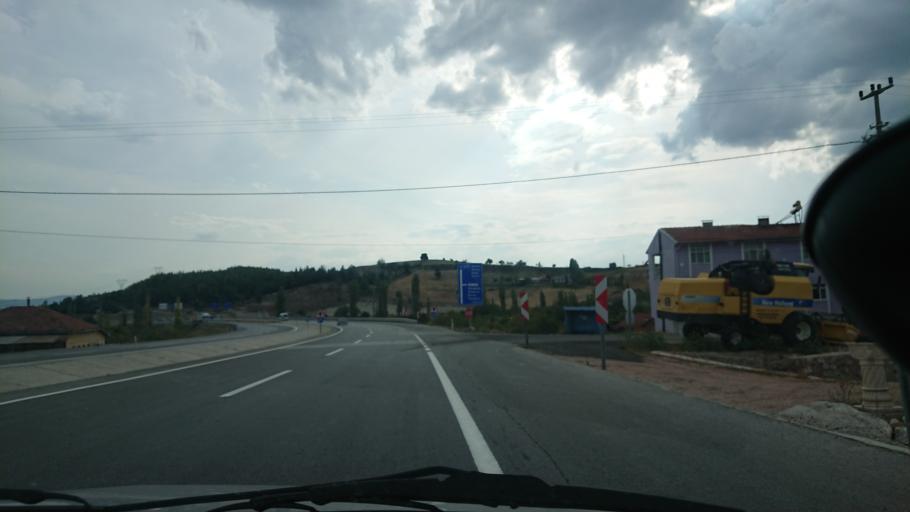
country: TR
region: Kuetahya
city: Gediz
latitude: 39.0342
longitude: 29.4180
